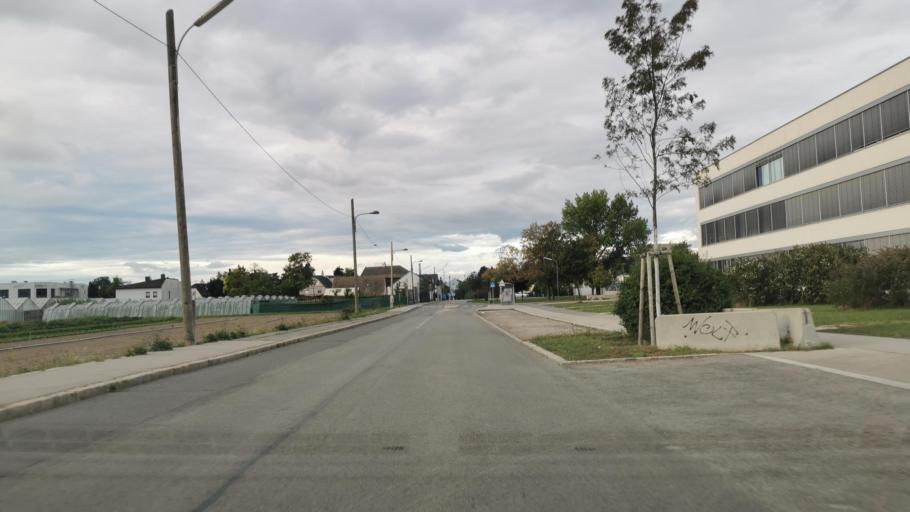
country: AT
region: Lower Austria
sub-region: Politischer Bezirk Wien-Umgebung
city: Gerasdorf bei Wien
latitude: 48.2314
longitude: 16.4707
